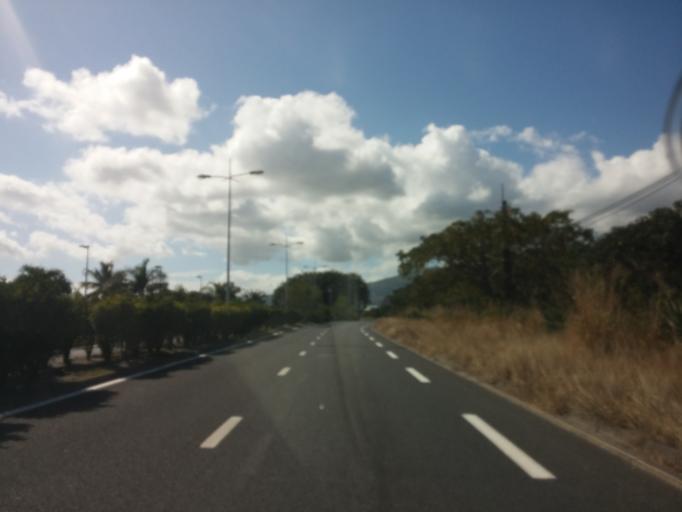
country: RE
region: Reunion
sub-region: Reunion
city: Le Port
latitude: -20.9508
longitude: 55.3000
